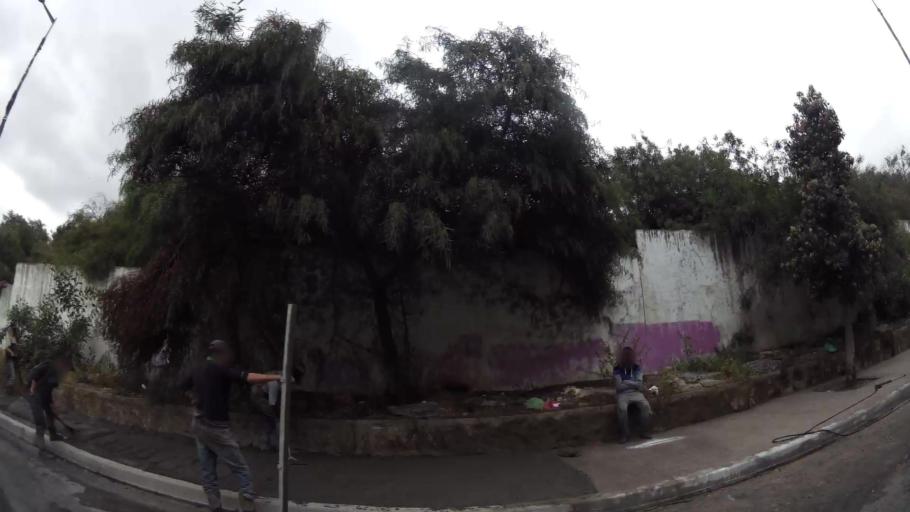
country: MA
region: Rabat-Sale-Zemmour-Zaer
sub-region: Rabat
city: Rabat
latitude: 33.9852
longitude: -6.8048
